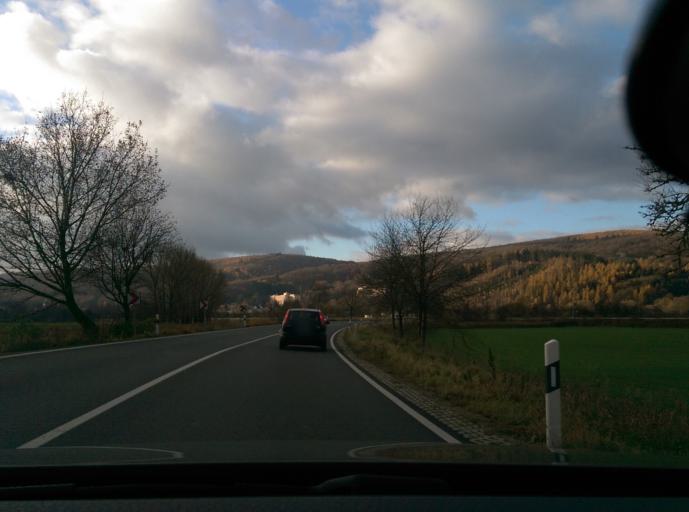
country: DE
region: Hesse
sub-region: Regierungsbezirk Kassel
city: Bad Sooden-Allendorf
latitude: 51.2843
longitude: 9.9669
